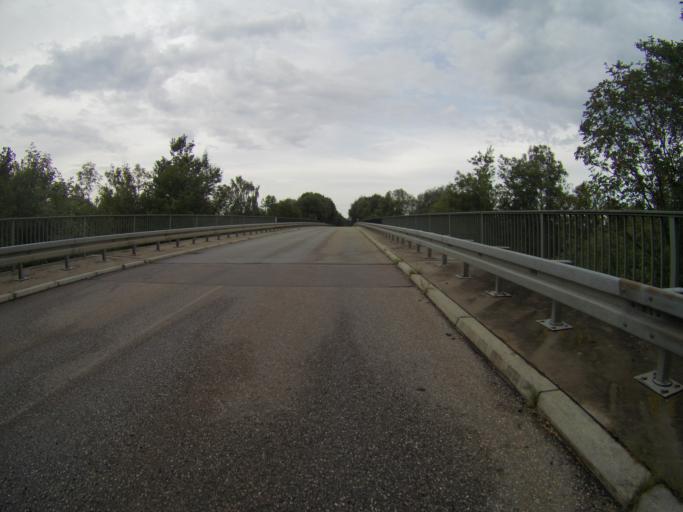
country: DE
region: Bavaria
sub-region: Upper Bavaria
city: Marzling
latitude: 48.3900
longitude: 11.7982
